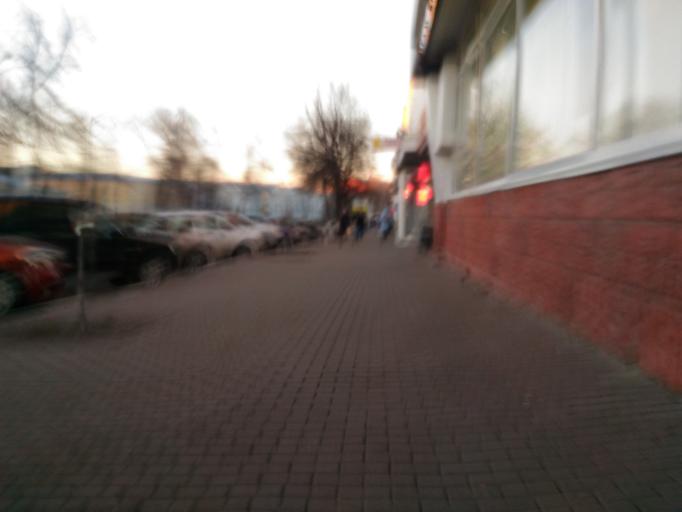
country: RU
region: Ulyanovsk
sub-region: Ulyanovskiy Rayon
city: Ulyanovsk
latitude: 54.3150
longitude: 48.3961
